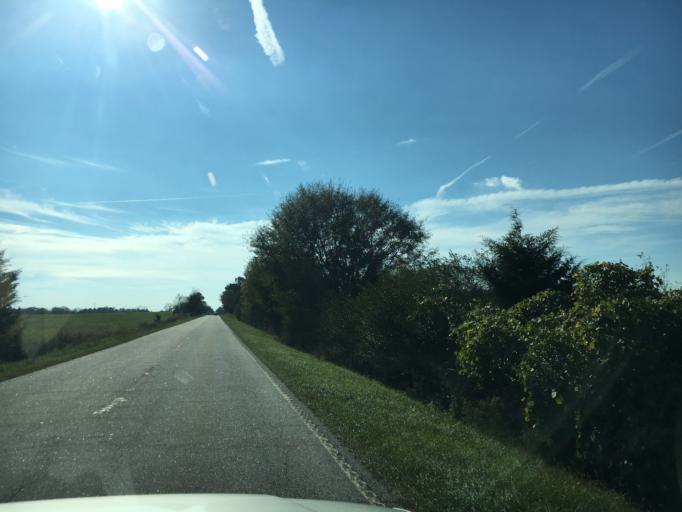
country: US
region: South Carolina
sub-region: Anderson County
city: Iva
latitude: 34.3633
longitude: -82.7179
